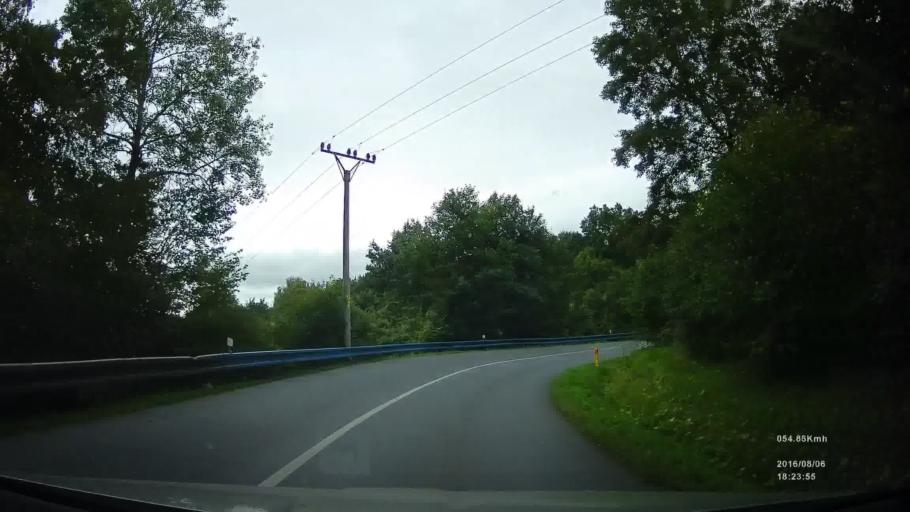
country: SK
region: Presovsky
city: Svidnik
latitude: 49.2981
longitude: 21.5694
